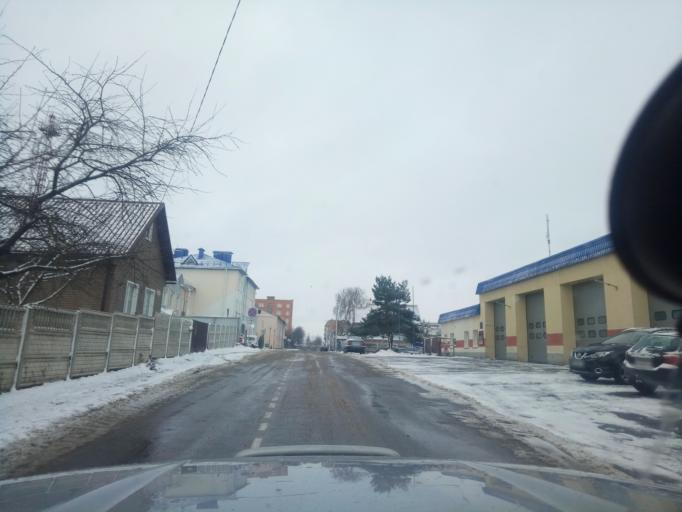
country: BY
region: Minsk
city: Kapyl'
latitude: 53.1530
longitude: 27.0855
